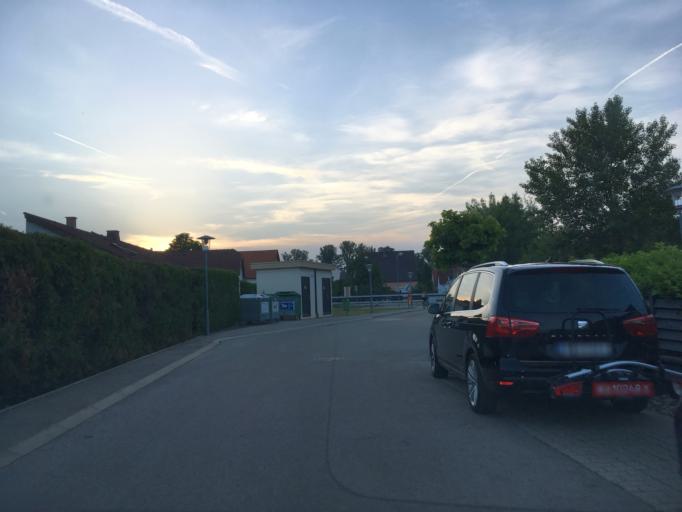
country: AT
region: Lower Austria
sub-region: Politischer Bezirk Baden
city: Teesdorf
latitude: 47.9474
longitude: 16.2814
